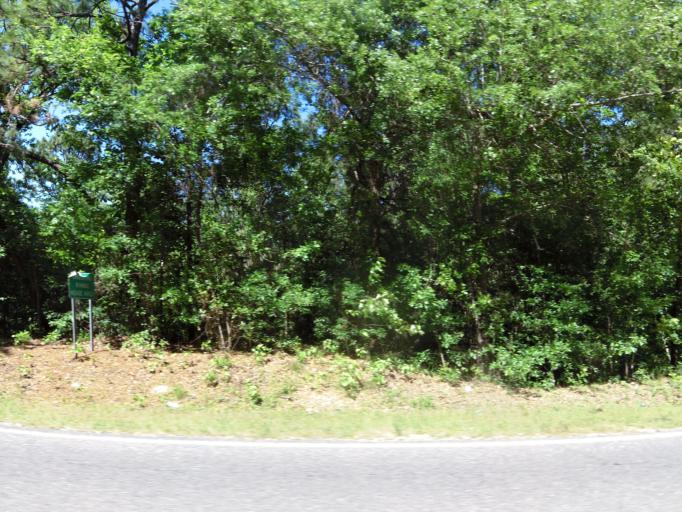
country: US
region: South Carolina
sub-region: Barnwell County
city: Williston
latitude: 33.4995
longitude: -81.5328
